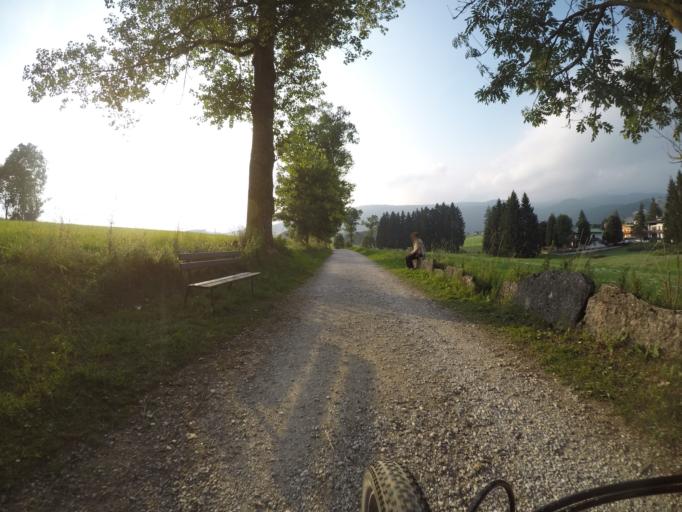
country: IT
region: Veneto
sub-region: Provincia di Vicenza
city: Asiago
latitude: 45.8783
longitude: 11.5034
